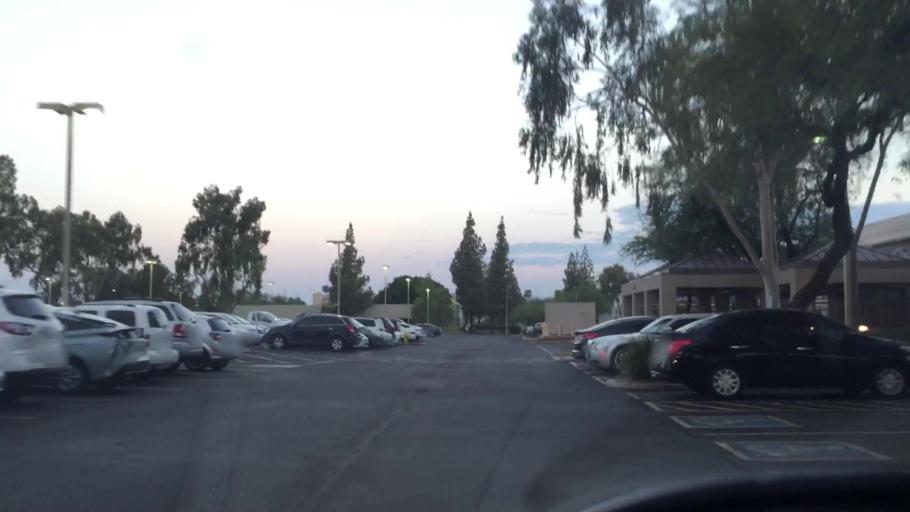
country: US
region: Arizona
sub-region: Maricopa County
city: Tempe Junction
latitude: 33.4105
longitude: -111.9658
